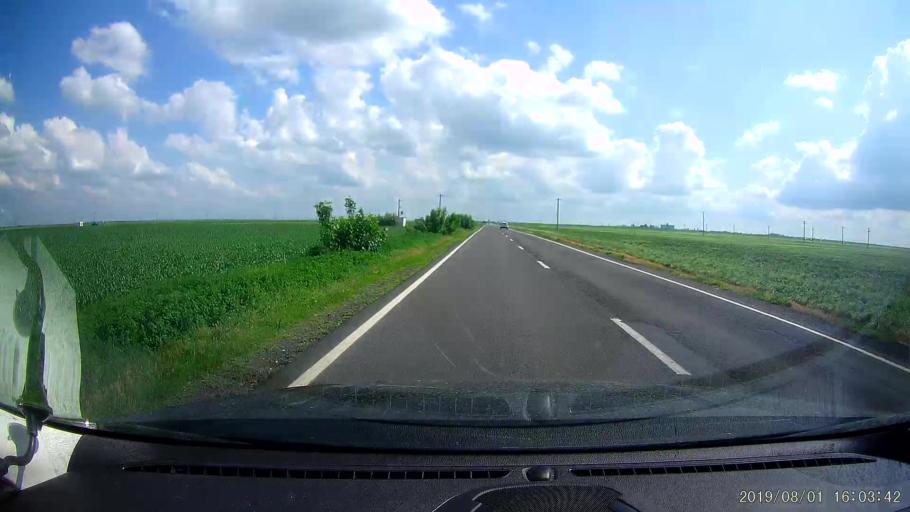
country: RO
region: Calarasi
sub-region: Comuna Dragalina
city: Drajna Noua
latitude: 44.4658
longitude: 27.3833
